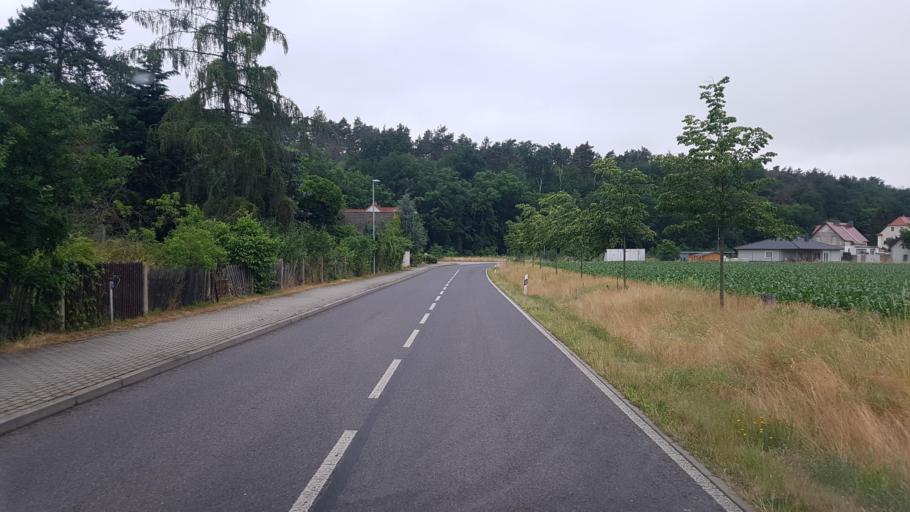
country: DE
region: Brandenburg
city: Schwarzbach
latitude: 51.4929
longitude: 13.9535
